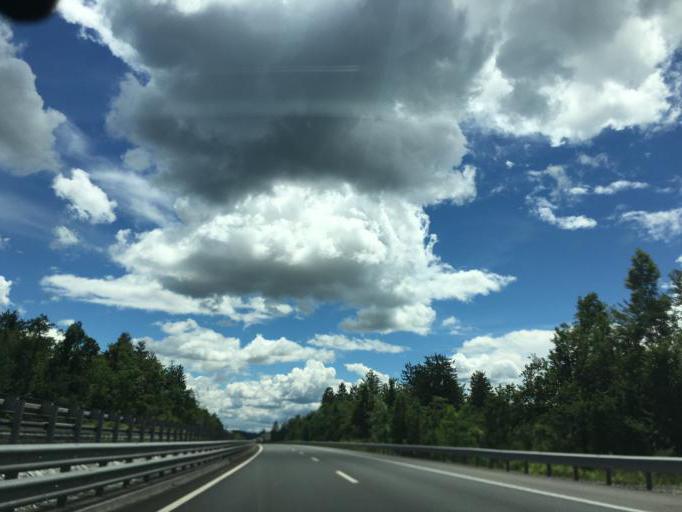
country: SI
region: Cerknica
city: Rakek
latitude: 45.8622
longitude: 14.2731
